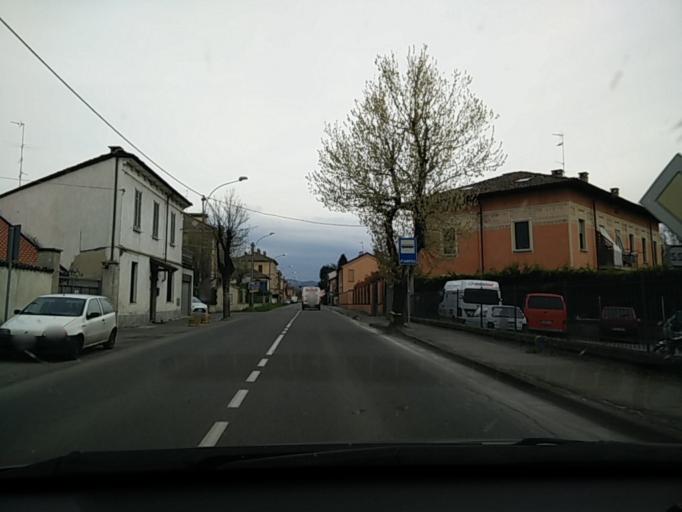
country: IT
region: Lombardy
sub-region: Provincia di Pavia
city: Rivanazzano
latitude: 44.9293
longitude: 9.0210
